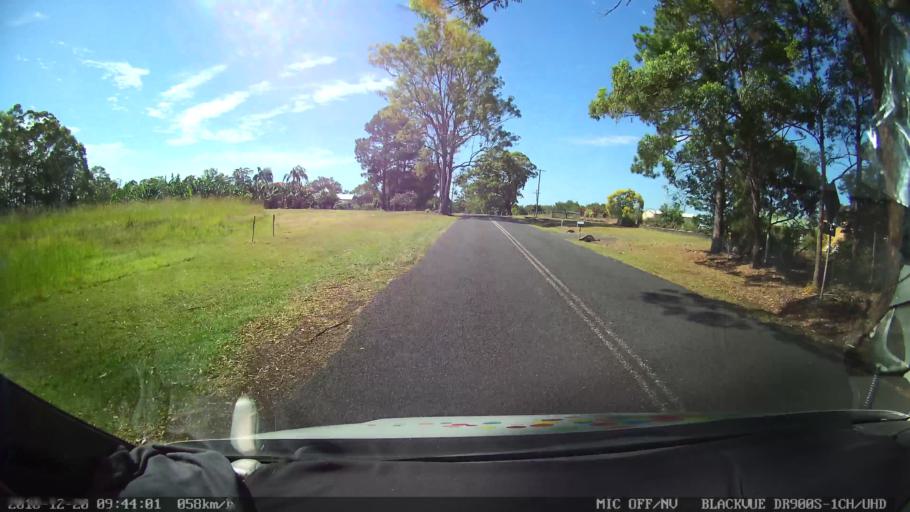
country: AU
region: New South Wales
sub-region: Lismore Municipality
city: Lismore
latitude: -28.7308
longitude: 153.2979
